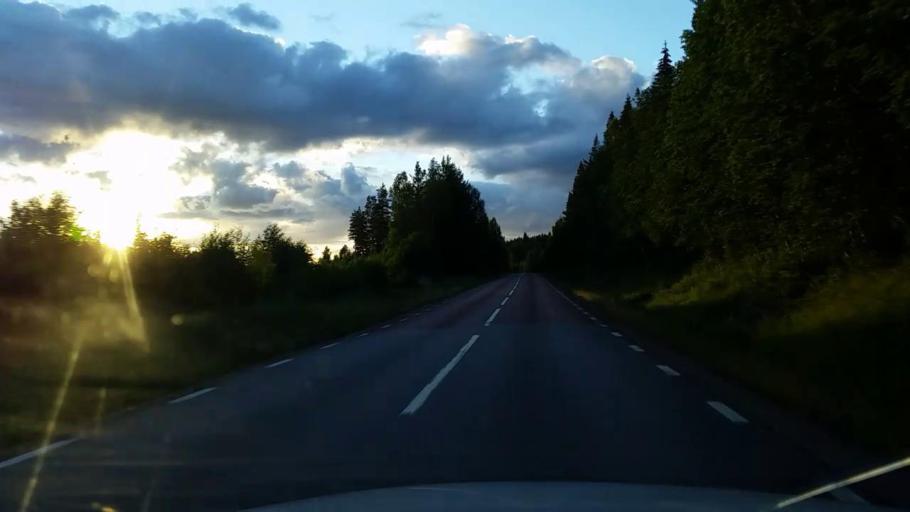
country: SE
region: Vaesternorrland
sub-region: Ange Kommun
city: Ange
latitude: 62.1486
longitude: 15.6835
